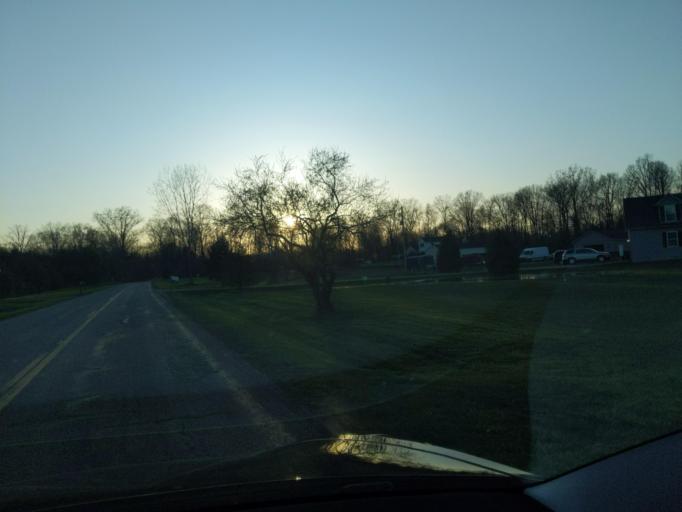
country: US
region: Michigan
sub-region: Ingham County
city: Stockbridge
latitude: 42.5029
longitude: -84.2557
